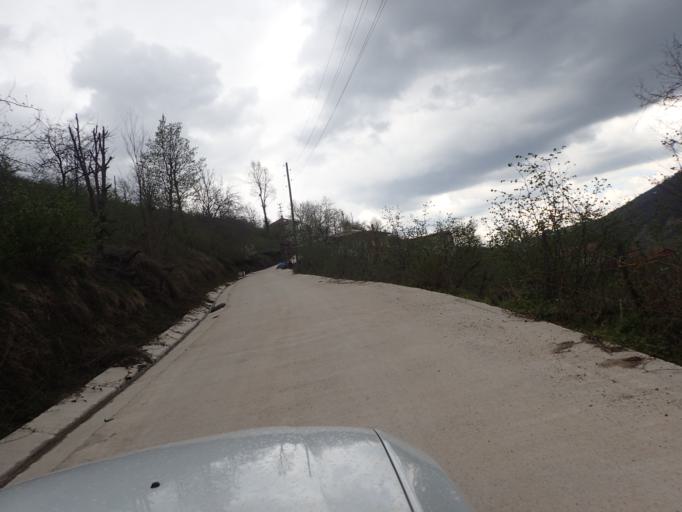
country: TR
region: Ordu
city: Korgan
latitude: 40.7642
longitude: 37.3197
